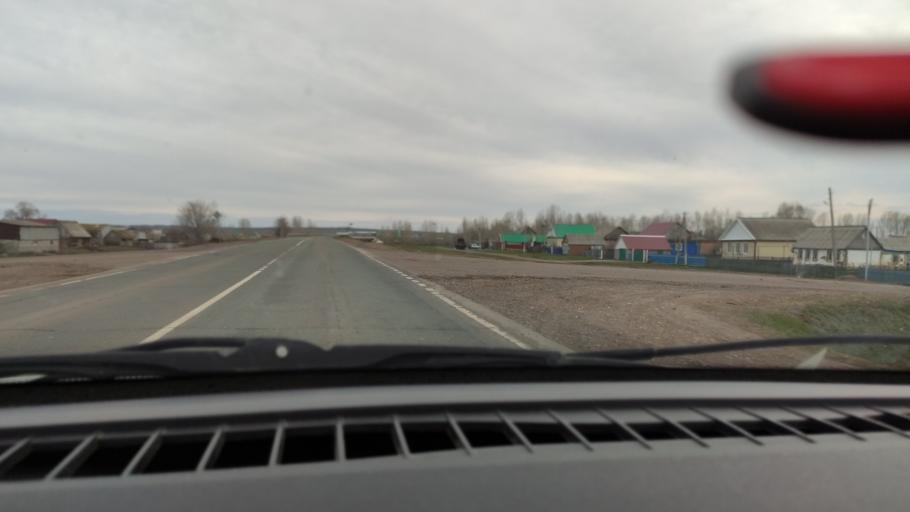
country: RU
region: Bashkortostan
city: Mayachnyy
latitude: 52.4328
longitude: 55.7910
